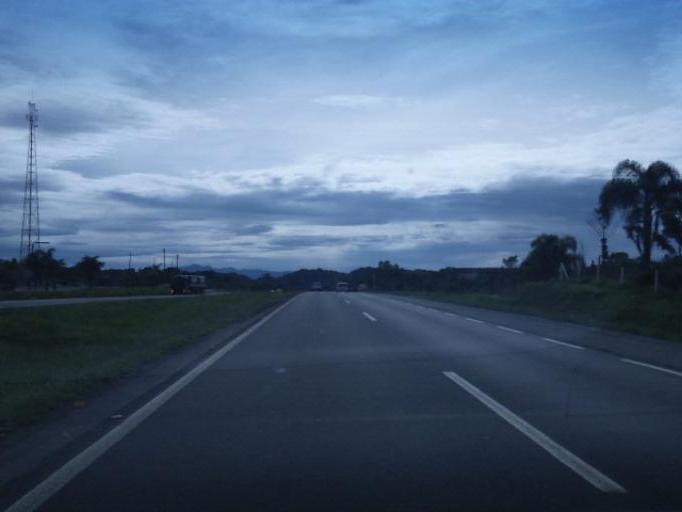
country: BR
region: Sao Paulo
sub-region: Cajati
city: Cajati
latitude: -24.9364
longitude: -48.2933
